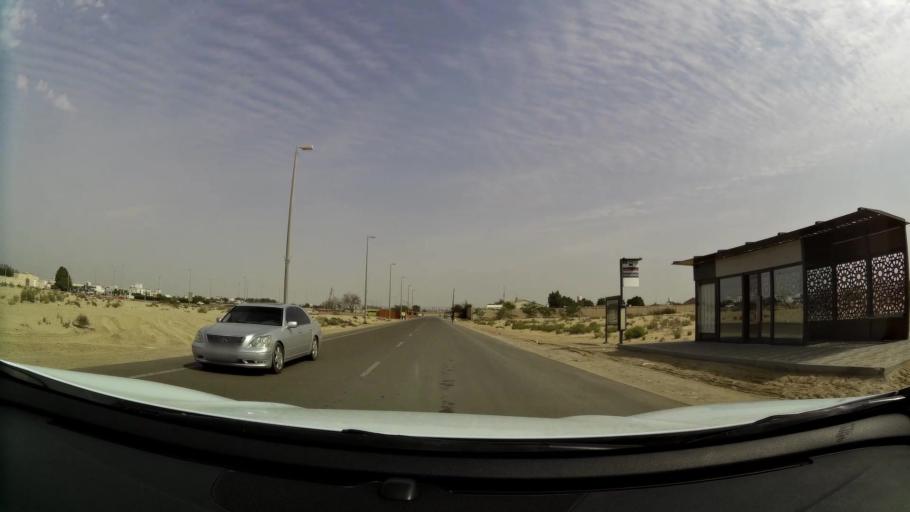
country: AE
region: Abu Dhabi
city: Abu Dhabi
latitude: 24.5641
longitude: 54.6816
